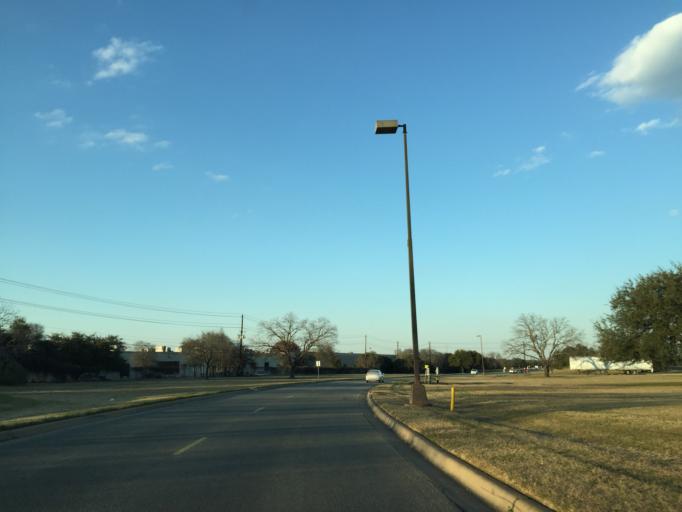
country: US
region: Texas
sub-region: Williamson County
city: Jollyville
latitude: 30.4332
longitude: -97.7580
